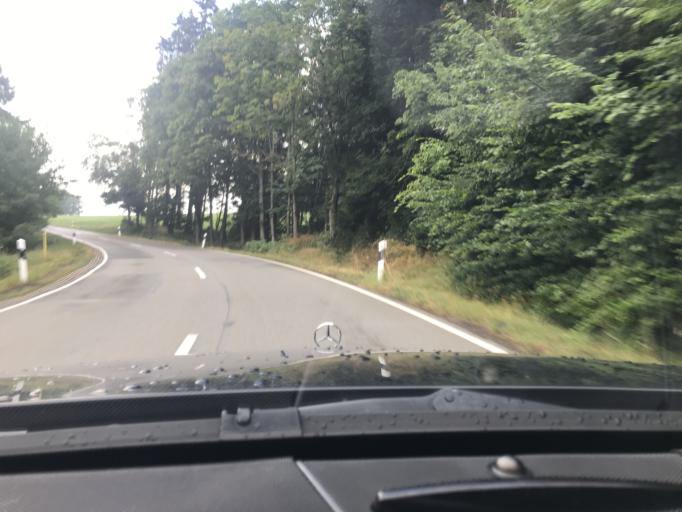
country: DE
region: Lower Saxony
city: Sankt Andreasberg
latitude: 51.7118
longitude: 10.5436
